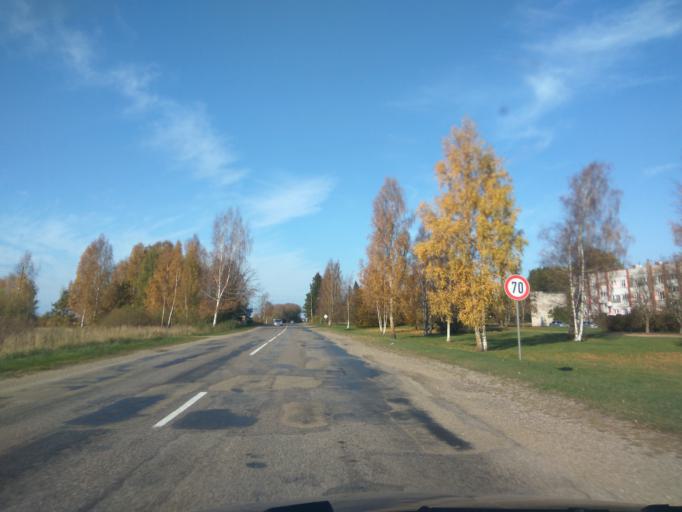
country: LV
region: Ventspils
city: Ventspils
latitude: 57.3034
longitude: 21.5601
